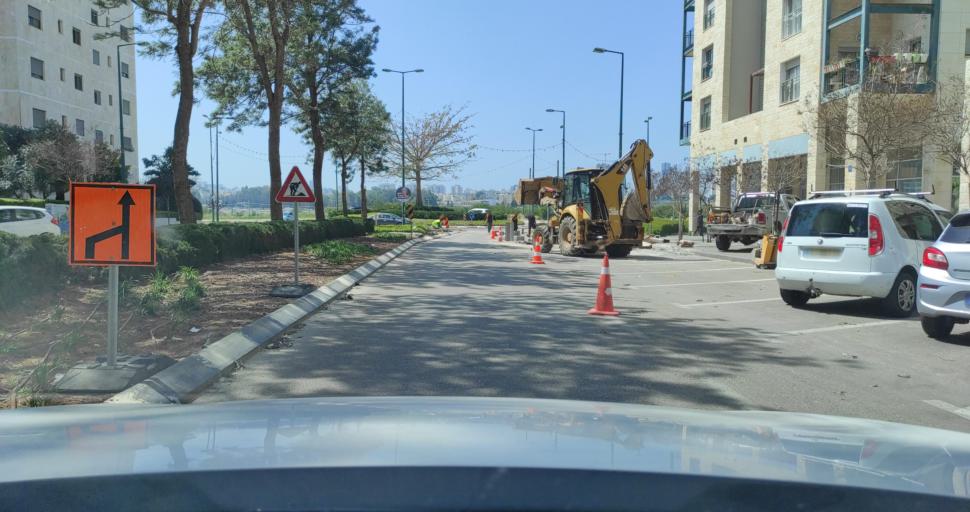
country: IL
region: Central District
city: Nordiyya
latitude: 32.3028
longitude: 34.8704
